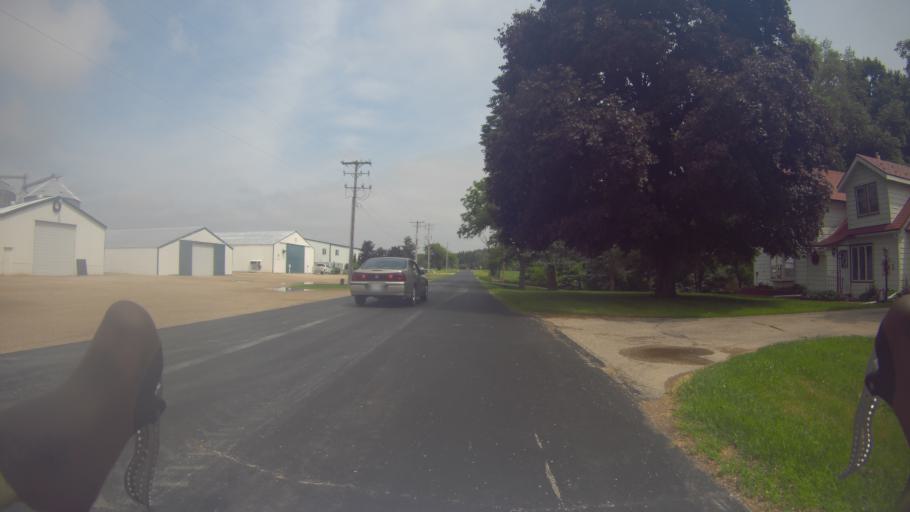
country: US
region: Wisconsin
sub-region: Rock County
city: Edgerton
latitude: 42.8906
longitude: -89.0402
